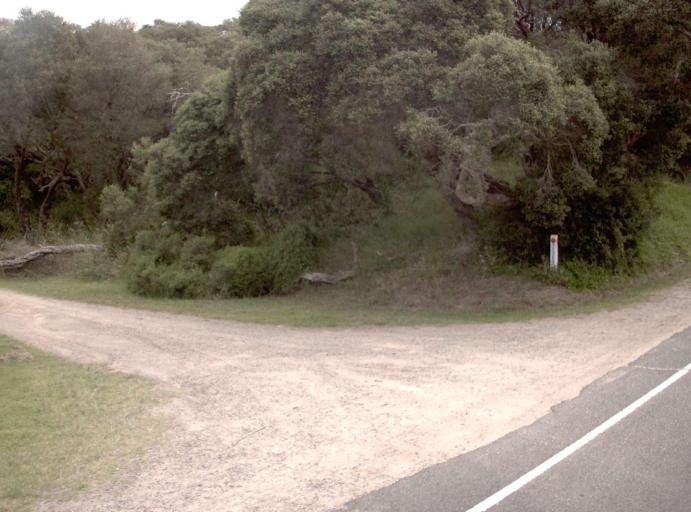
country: AU
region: Victoria
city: Rye
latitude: -38.3672
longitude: 144.8076
